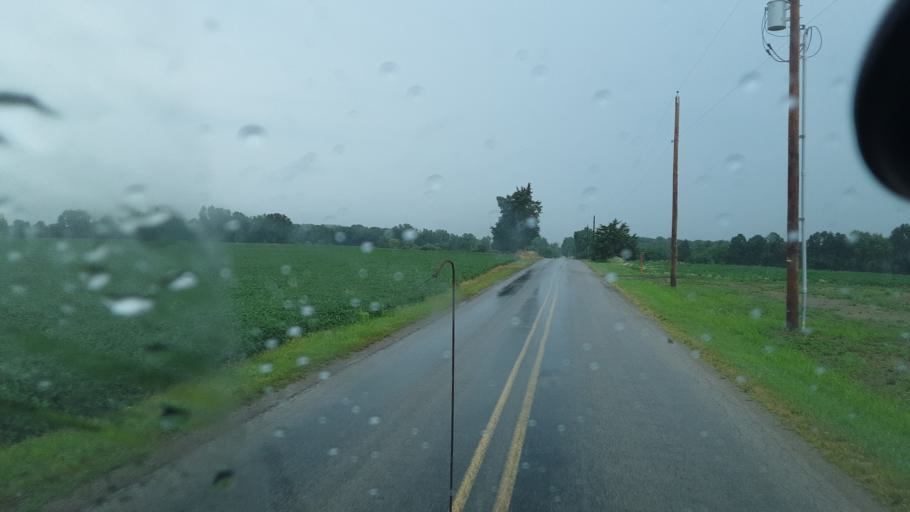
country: US
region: Ohio
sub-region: Williams County
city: Edgerton
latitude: 41.4807
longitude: -84.8145
